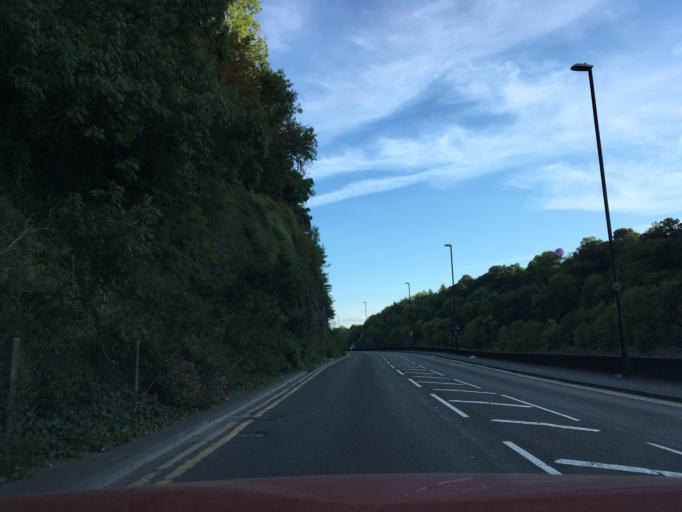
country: GB
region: England
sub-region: Bristol
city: Bristol
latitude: 51.4548
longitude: -2.6269
